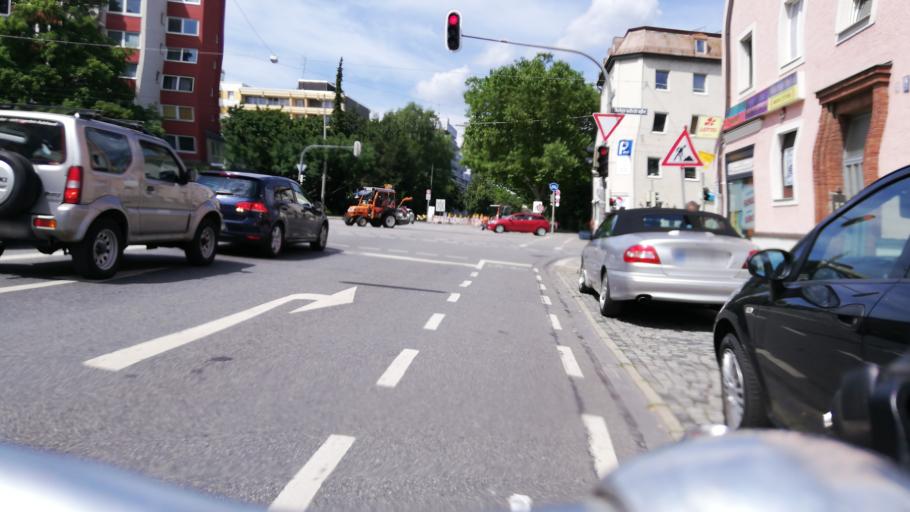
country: DE
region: Bavaria
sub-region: Upper Bavaria
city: Munich
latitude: 48.1672
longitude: 11.5744
